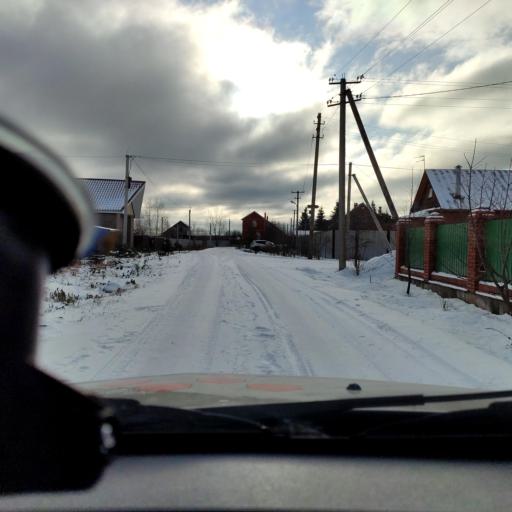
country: RU
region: Bashkortostan
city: Avdon
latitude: 54.7859
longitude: 55.7210
